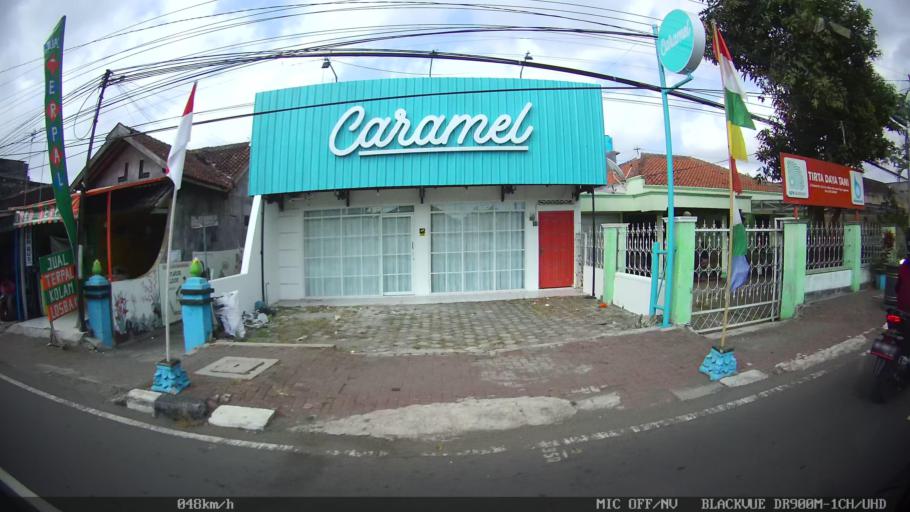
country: ID
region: Daerah Istimewa Yogyakarta
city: Srandakan
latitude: -7.8651
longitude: 110.1536
